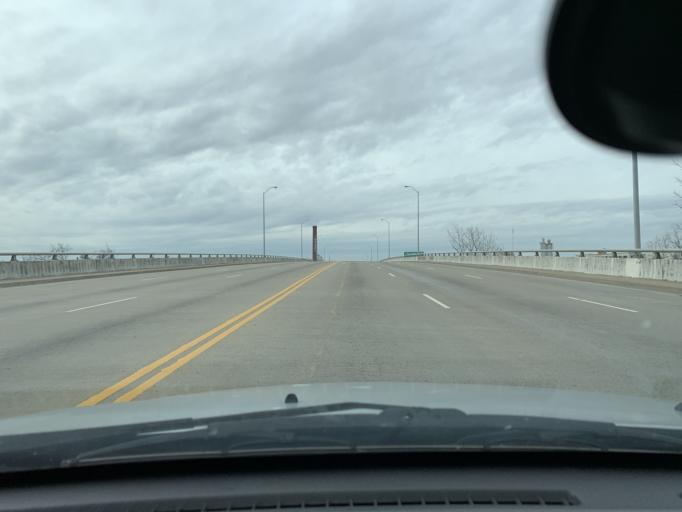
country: US
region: Tennessee
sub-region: Davidson County
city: Nashville
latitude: 36.1765
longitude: -86.7780
